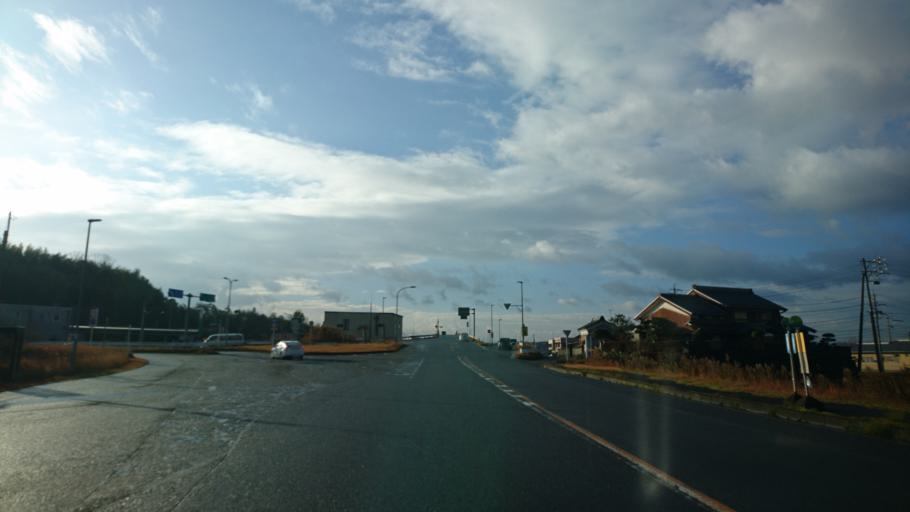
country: JP
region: Mie
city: Ueno-ebisumachi
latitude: 34.7502
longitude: 136.1226
